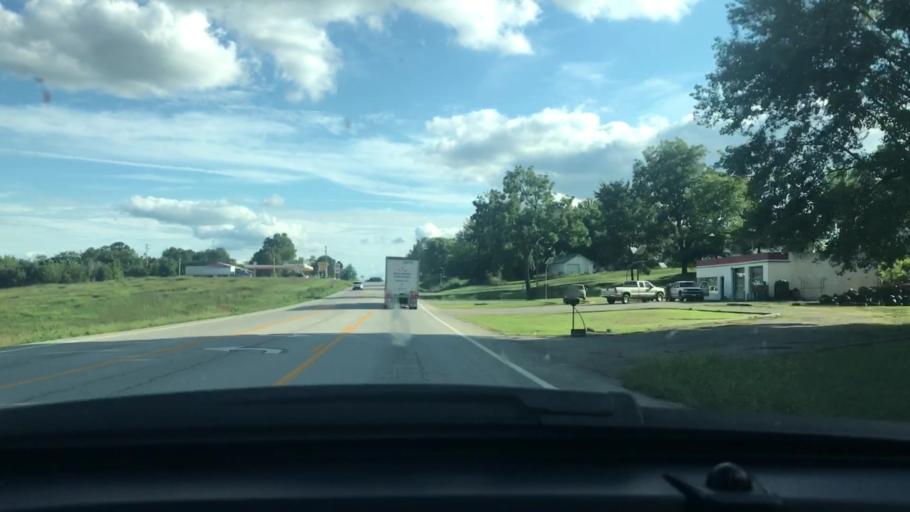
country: US
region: Missouri
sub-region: Oregon County
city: Thayer
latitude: 36.5974
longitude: -91.6440
